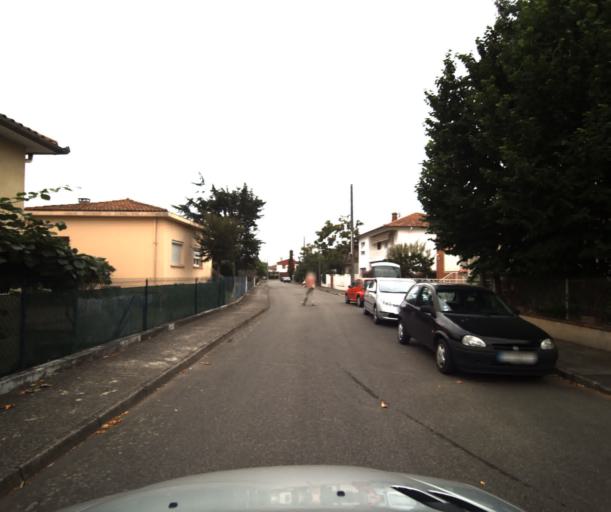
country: FR
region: Midi-Pyrenees
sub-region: Departement de la Haute-Garonne
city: Portet-sur-Garonne
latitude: 43.5249
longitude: 1.4041
